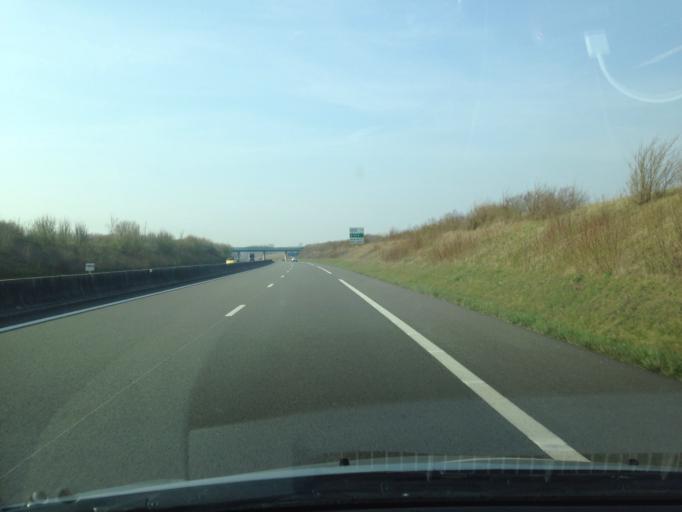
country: FR
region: Picardie
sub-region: Departement de la Somme
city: Nouvion
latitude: 50.2596
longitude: 1.7468
